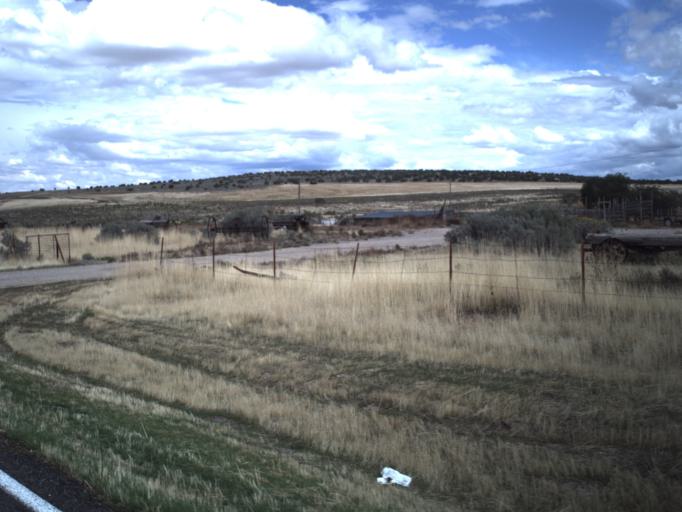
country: US
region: Utah
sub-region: Millard County
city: Fillmore
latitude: 38.9891
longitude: -112.4112
